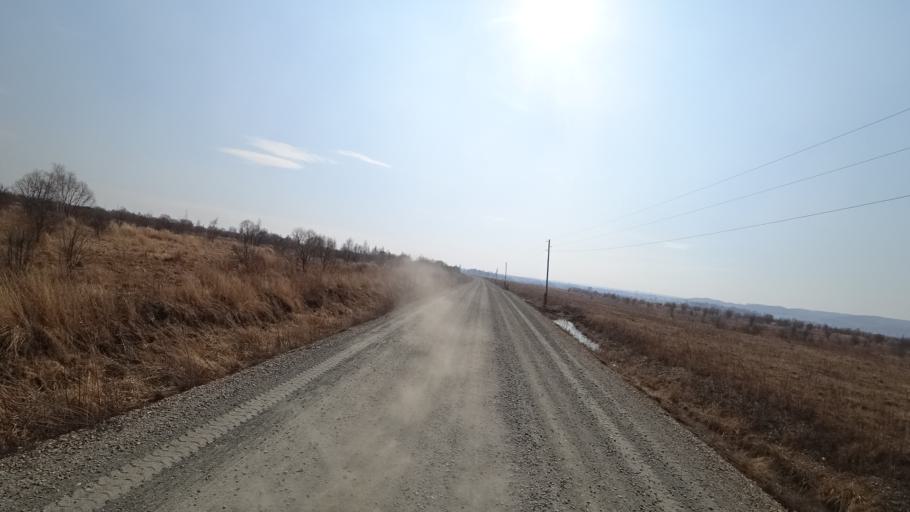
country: RU
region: Amur
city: Novobureyskiy
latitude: 49.8126
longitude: 129.9717
